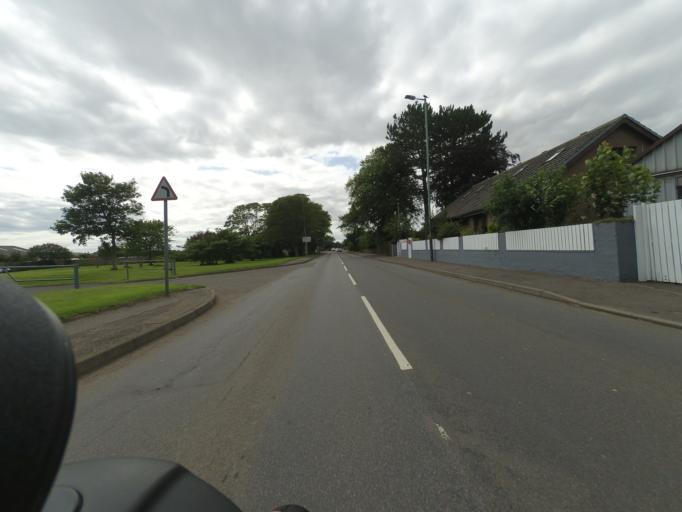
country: GB
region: Scotland
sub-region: Angus
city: Montrose
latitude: 56.7279
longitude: -2.4629
